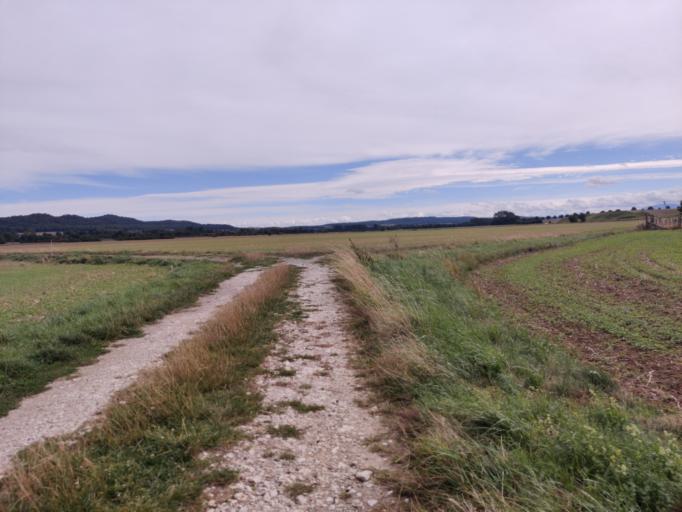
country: DE
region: Lower Saxony
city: Alt Wallmoden
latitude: 52.0164
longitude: 10.3411
